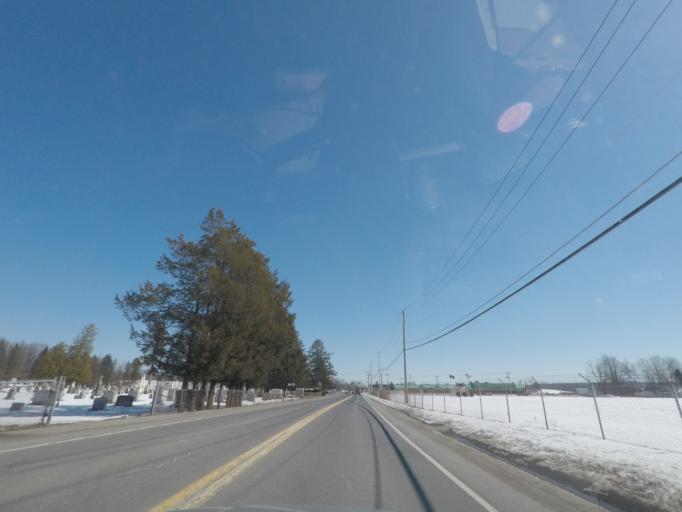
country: US
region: New York
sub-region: Saratoga County
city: Stillwater
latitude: 42.9075
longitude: -73.5875
